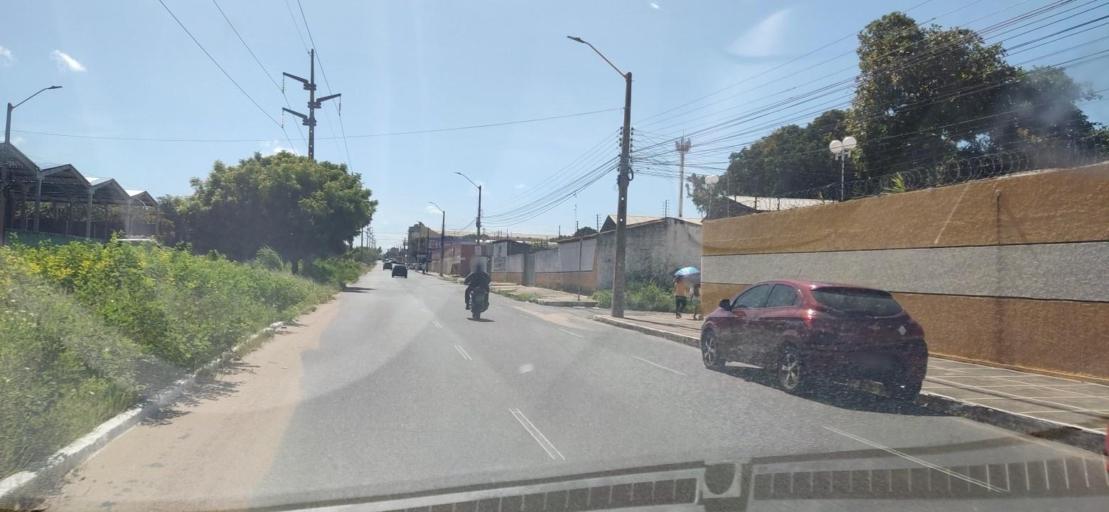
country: BR
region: Piaui
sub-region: Teresina
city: Teresina
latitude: -5.1216
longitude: -42.8069
